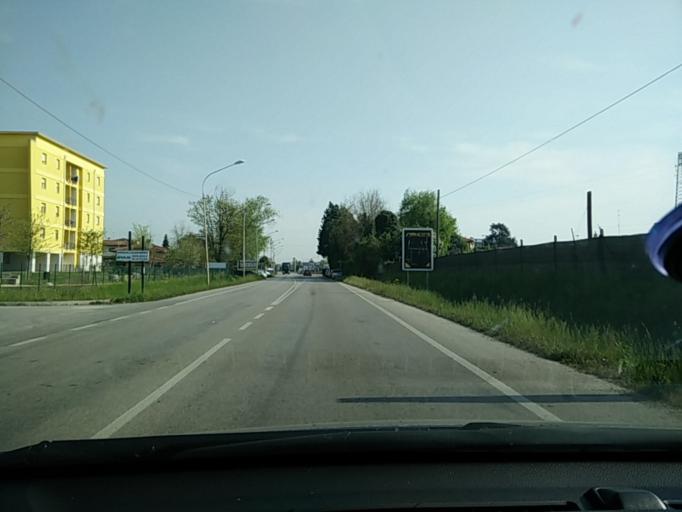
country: IT
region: Friuli Venezia Giulia
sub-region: Provincia di Pordenone
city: Azzano Decimo
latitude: 45.9276
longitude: 12.6434
